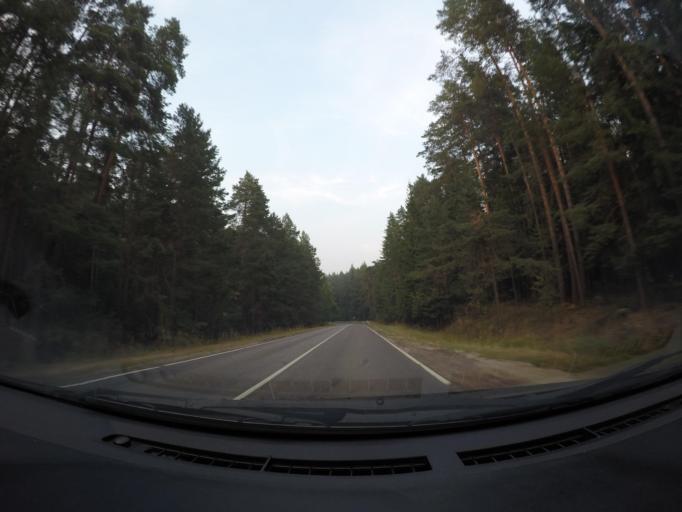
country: RU
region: Moskovskaya
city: Imeni Tsyurupy
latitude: 55.5027
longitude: 38.7101
